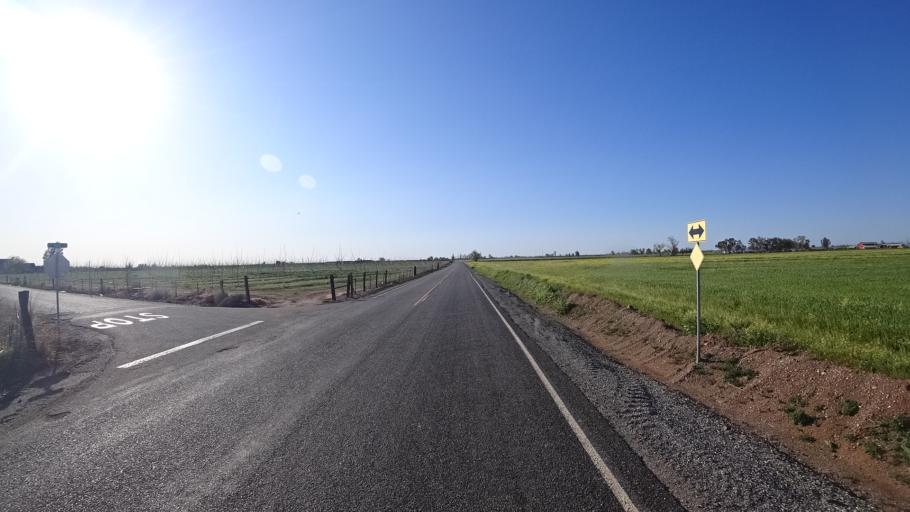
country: US
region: California
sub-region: Glenn County
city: Orland
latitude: 39.7826
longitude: -122.1174
